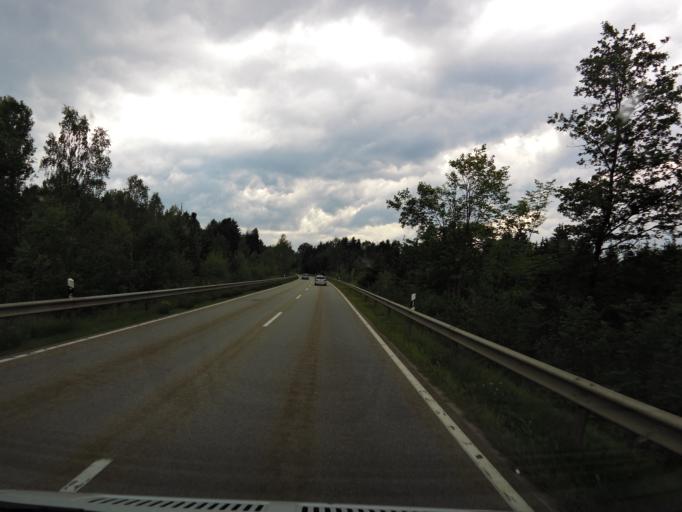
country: DE
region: Bavaria
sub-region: Lower Bavaria
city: Neukirchen vorm Wald
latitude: 48.6929
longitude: 13.4034
